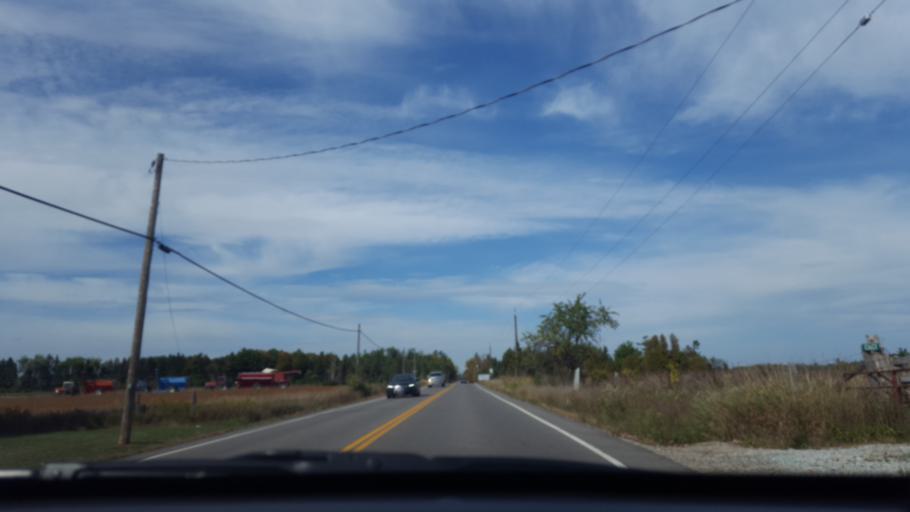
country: CA
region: Ontario
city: Vaughan
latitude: 43.8543
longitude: -79.5897
